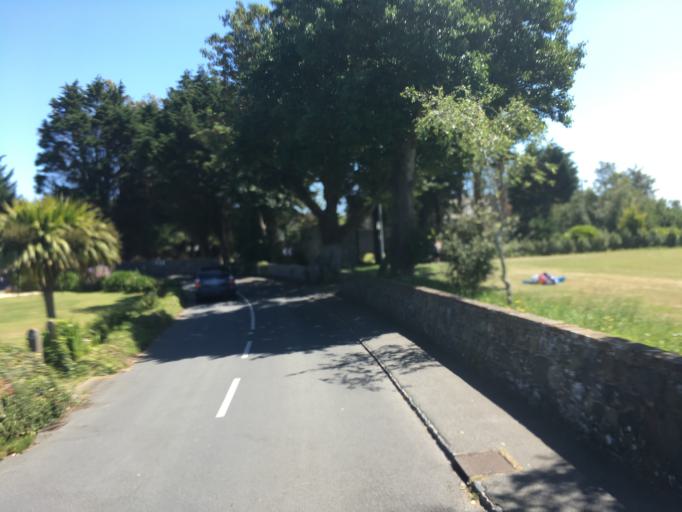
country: GG
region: St Peter Port
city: Saint Peter Port
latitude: 49.4887
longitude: -2.5124
